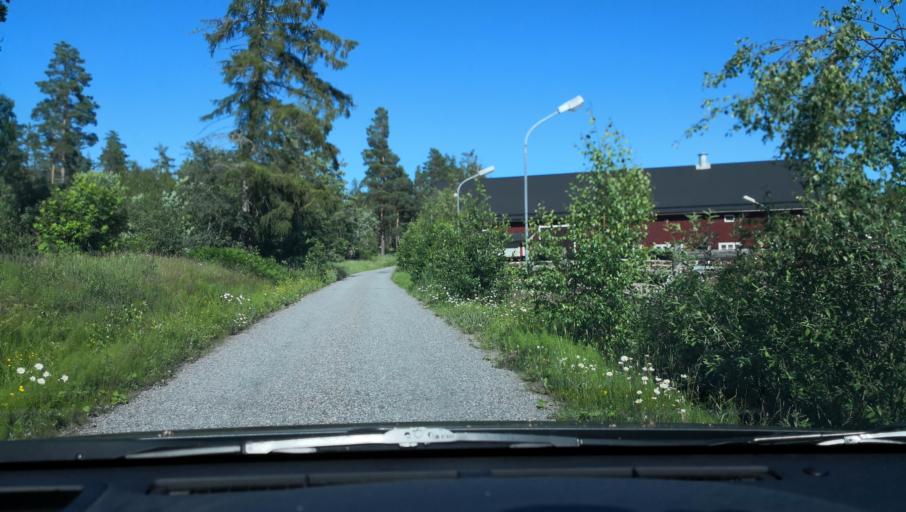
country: SE
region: Soedermanland
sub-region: Eskilstuna Kommun
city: Eskilstuna
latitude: 59.3288
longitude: 16.5895
